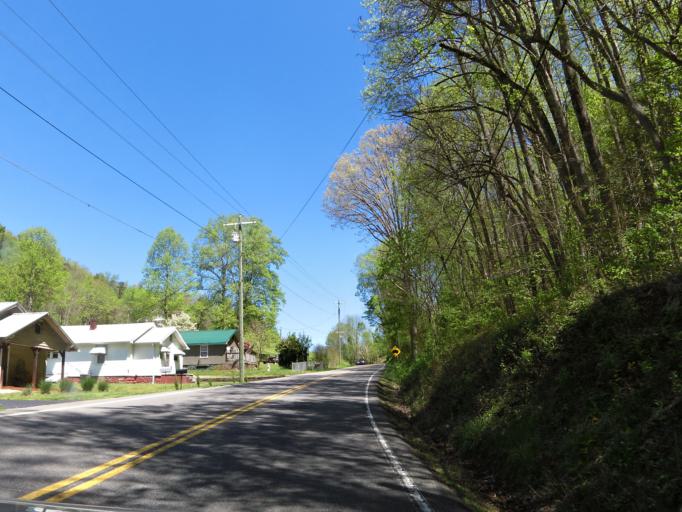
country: US
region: Tennessee
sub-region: Unicoi County
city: Erwin
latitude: 36.1501
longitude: -82.4311
